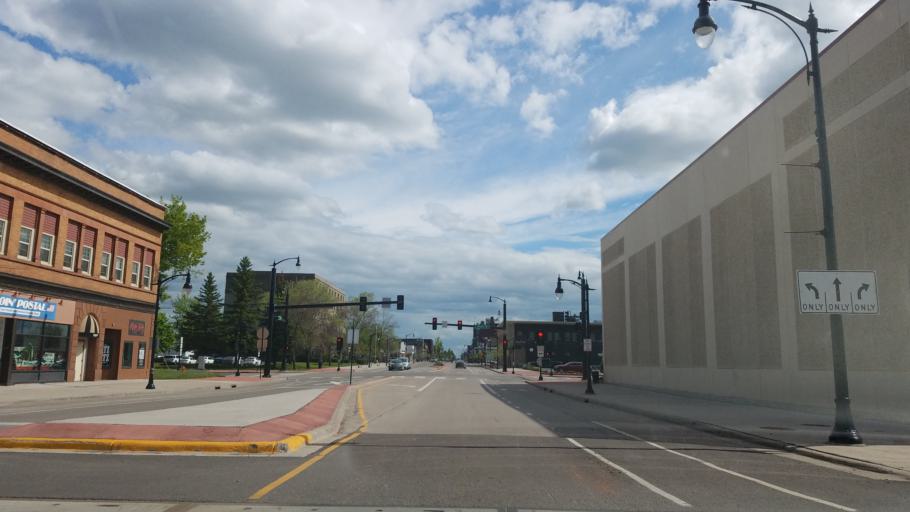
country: US
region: Wisconsin
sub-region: Douglas County
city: Superior
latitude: 46.7287
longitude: -92.1040
